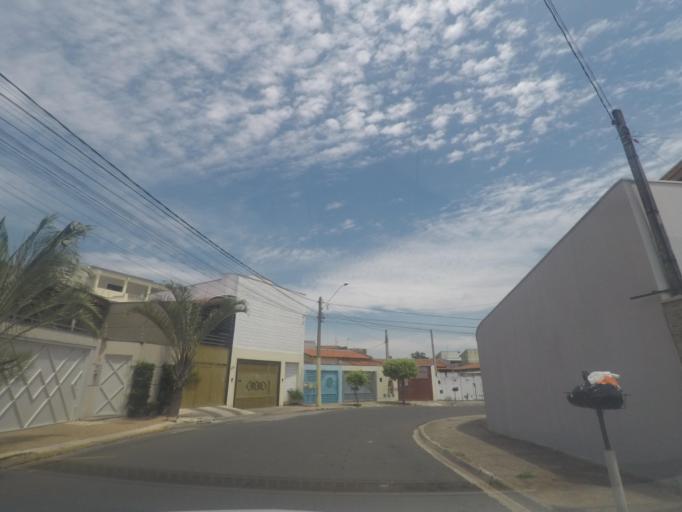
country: BR
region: Sao Paulo
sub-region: Sumare
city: Sumare
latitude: -22.8001
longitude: -47.2764
